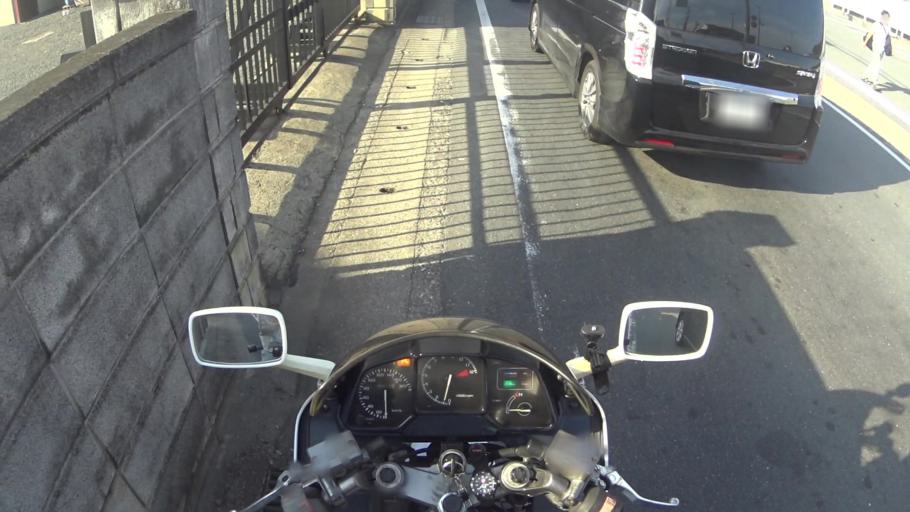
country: JP
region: Kyoto
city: Muko
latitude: 34.9266
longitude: 135.7228
